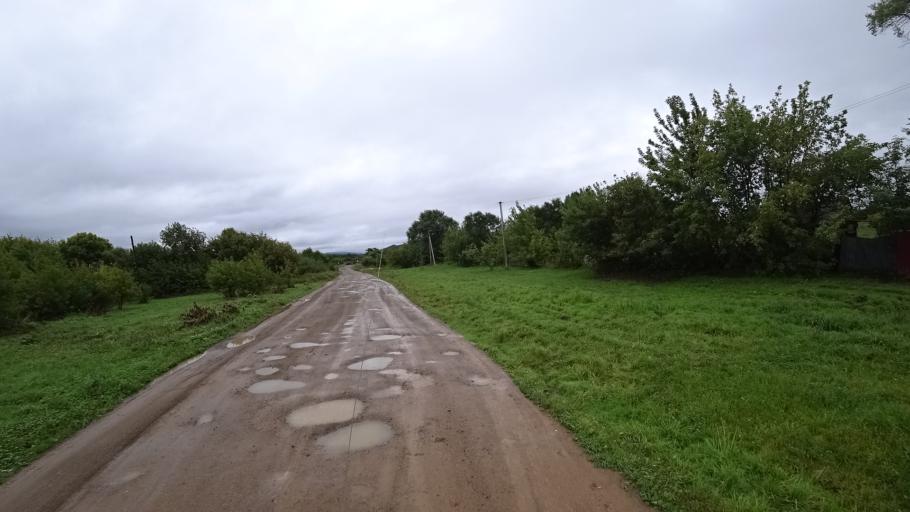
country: RU
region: Primorskiy
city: Monastyrishche
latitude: 44.2771
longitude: 132.4212
